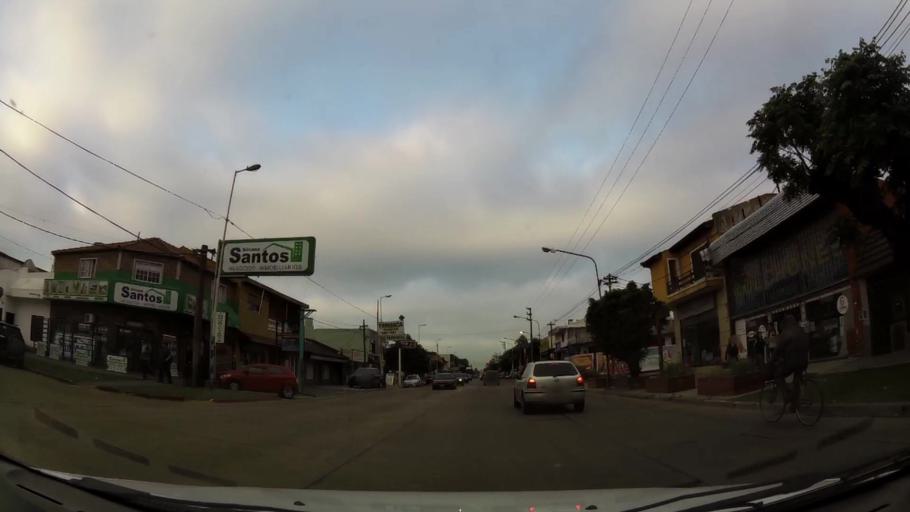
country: AR
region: Buenos Aires
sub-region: Partido de Moron
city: Moron
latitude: -34.6592
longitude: -58.5927
